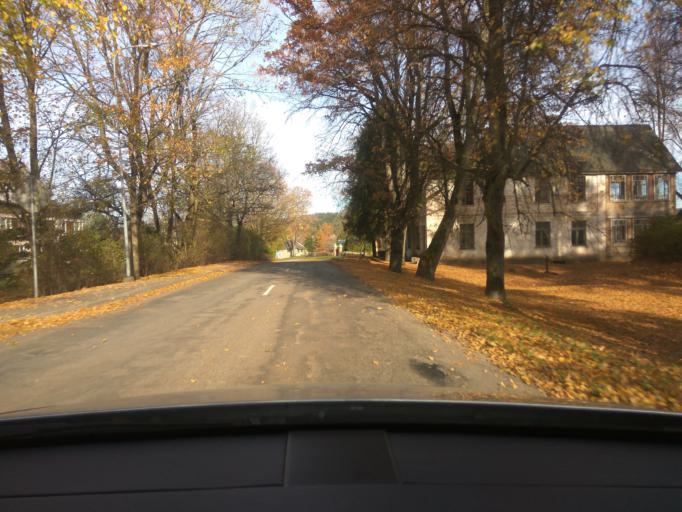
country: LV
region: Alsunga
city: Alsunga
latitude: 57.0159
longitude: 21.6881
